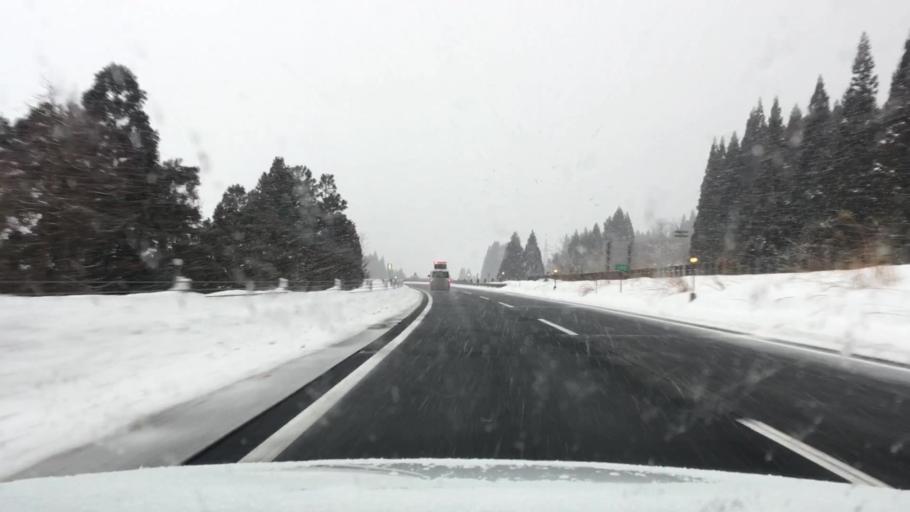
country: JP
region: Akita
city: Hanawa
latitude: 40.1472
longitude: 140.8077
